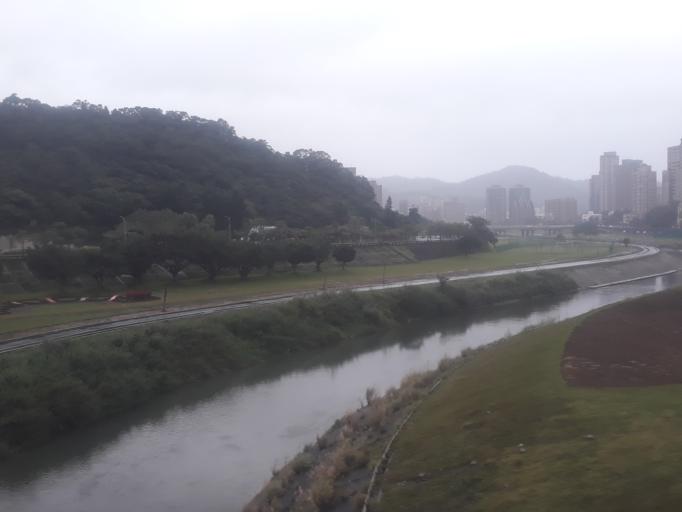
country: TW
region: Taipei
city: Taipei
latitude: 24.9979
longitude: 121.5752
